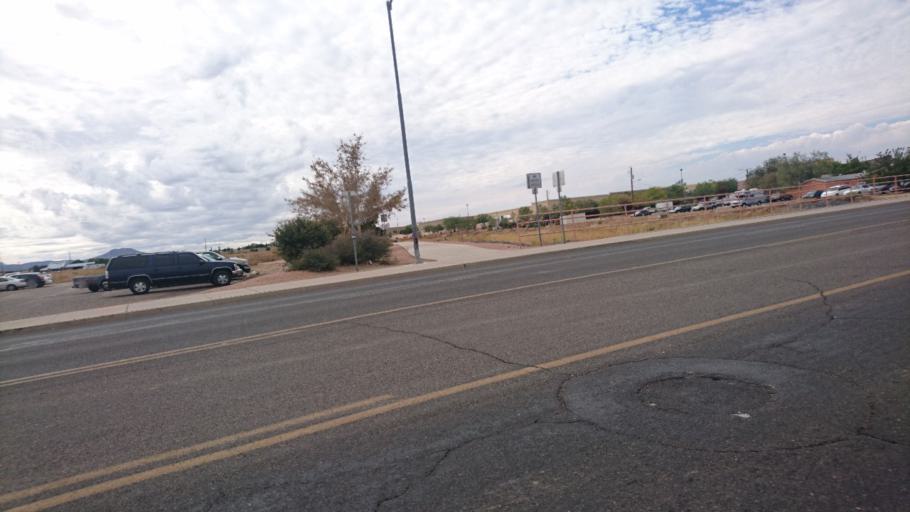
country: US
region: Arizona
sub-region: Mohave County
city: New Kingman-Butler
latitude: 35.2249
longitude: -114.0305
